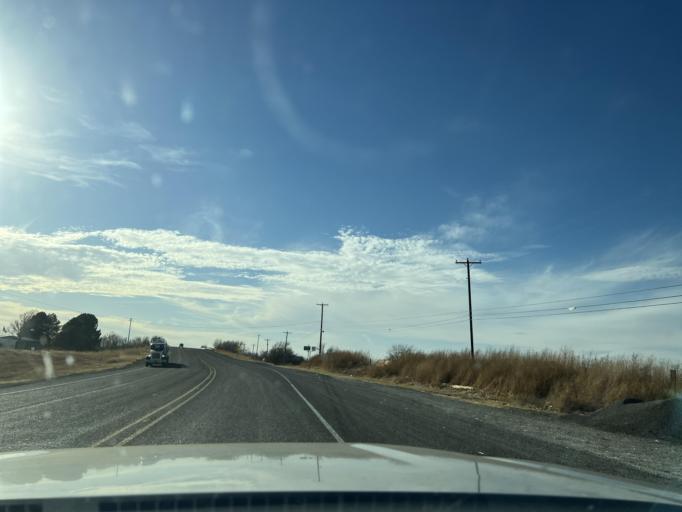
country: US
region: Texas
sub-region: Scurry County
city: Snyder
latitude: 32.7045
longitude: -100.8705
